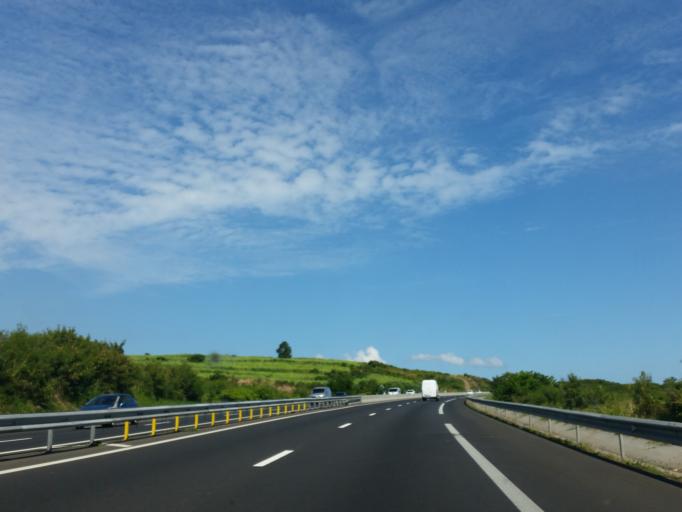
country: RE
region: Reunion
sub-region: Reunion
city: Saint-Paul
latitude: -21.0577
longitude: 55.2493
